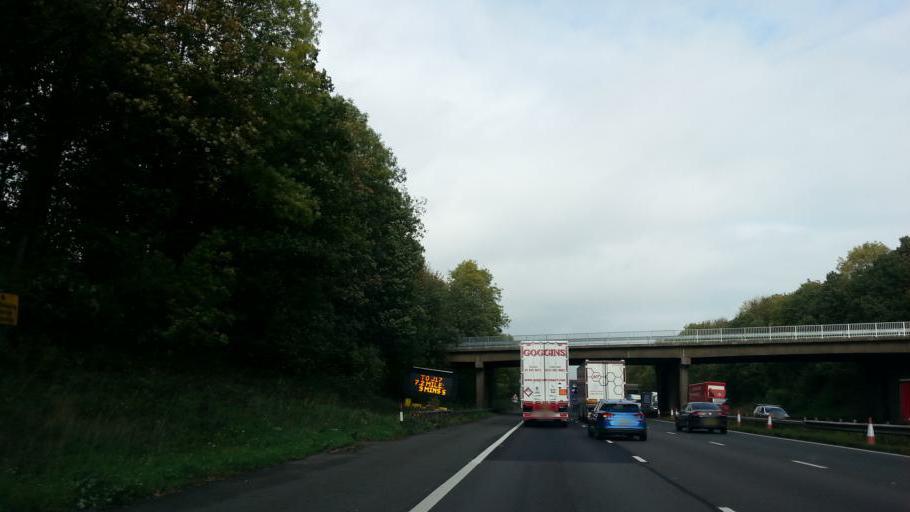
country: GB
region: England
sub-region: Staffordshire
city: Audley
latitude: 53.0488
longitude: -2.3308
